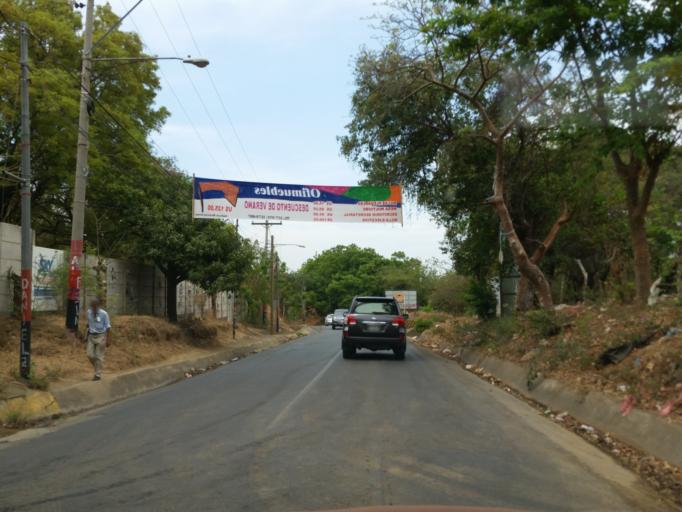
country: NI
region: Managua
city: Managua
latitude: 12.0982
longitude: -86.2486
